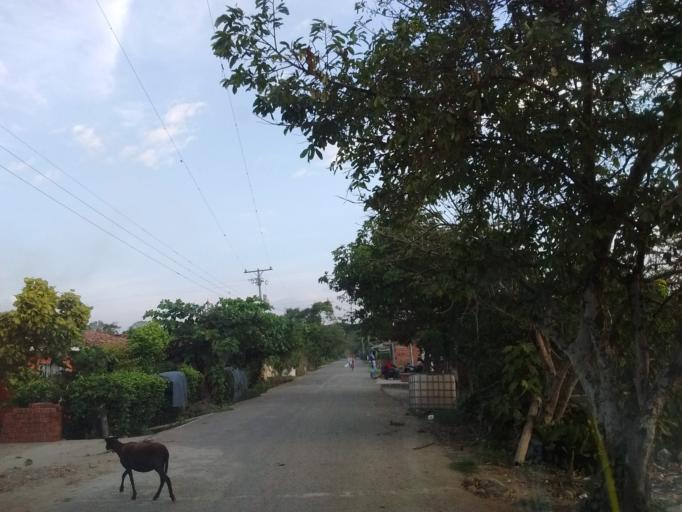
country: CO
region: Cauca
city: Puerto Tejada
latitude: 3.2198
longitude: -76.4433
